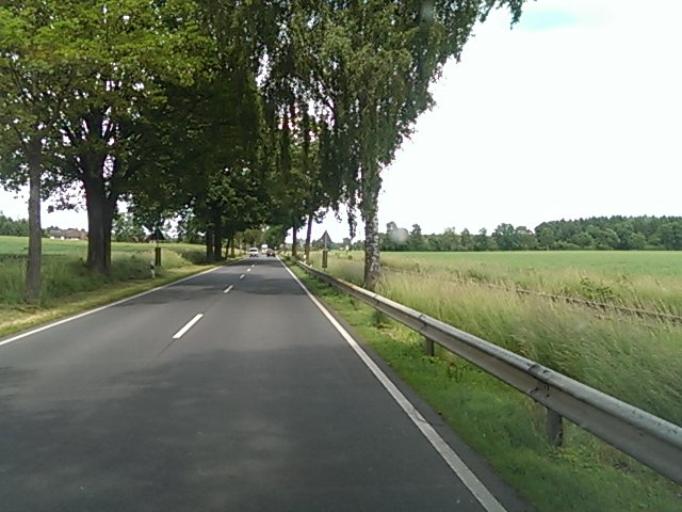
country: DE
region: Lower Saxony
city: Hermannsburg
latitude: 52.7950
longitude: 10.0465
